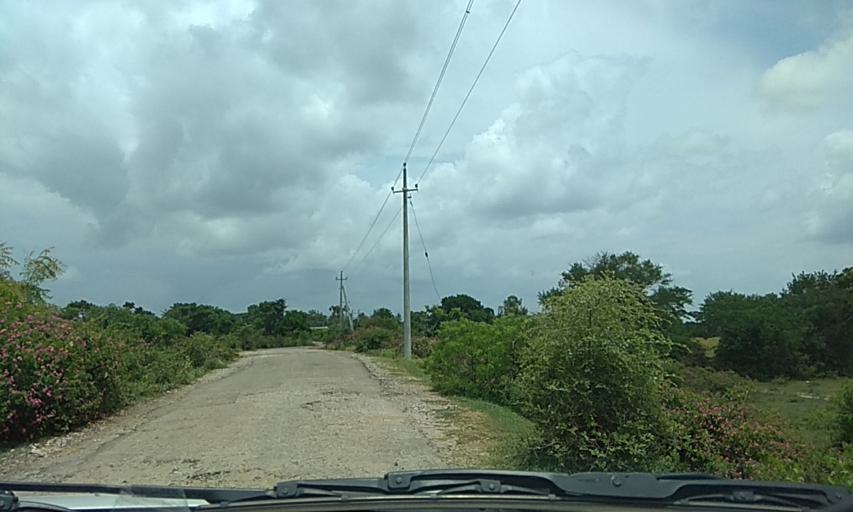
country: IN
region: Karnataka
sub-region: Chamrajnagar
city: Gundlupet
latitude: 11.8848
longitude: 76.6858
